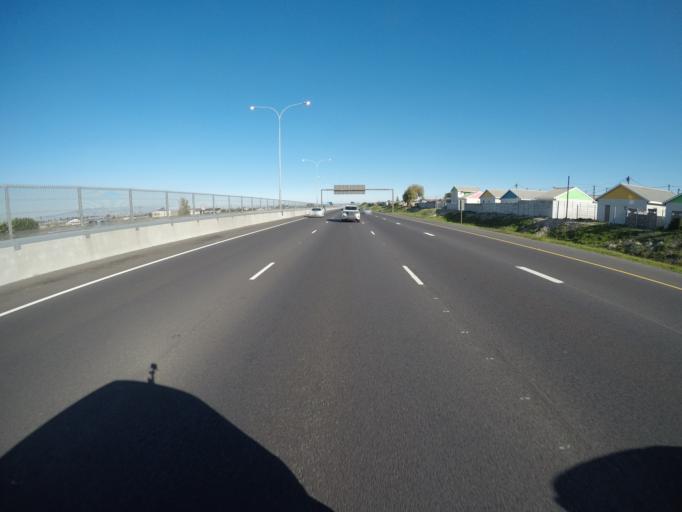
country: ZA
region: Western Cape
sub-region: City of Cape Town
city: Kraaifontein
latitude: -33.9625
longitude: 18.6557
